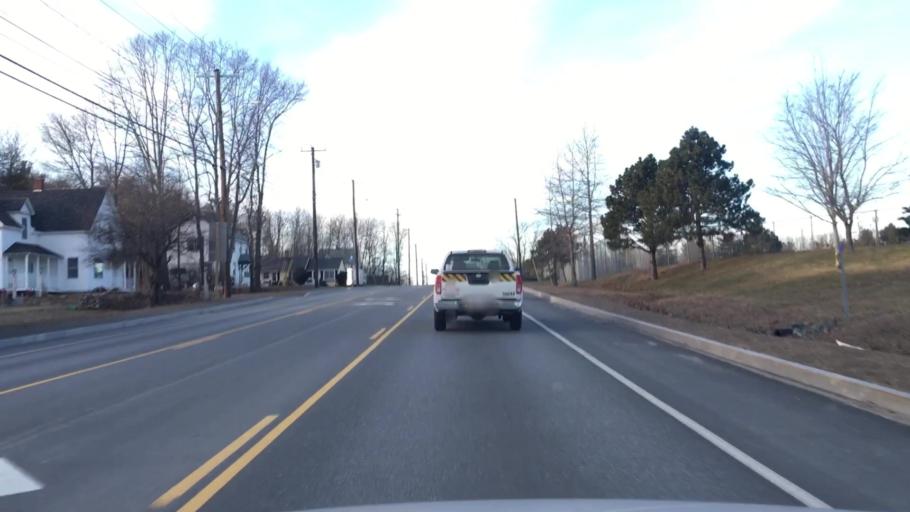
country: US
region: Maine
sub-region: Hancock County
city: Ellsworth
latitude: 44.5546
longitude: -68.4312
